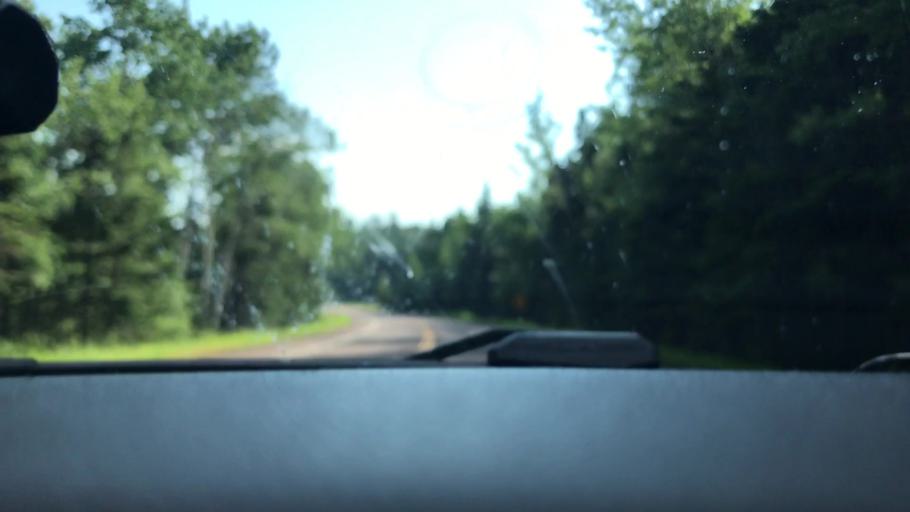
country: US
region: Minnesota
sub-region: Cook County
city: Grand Marais
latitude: 47.8402
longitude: -89.9701
